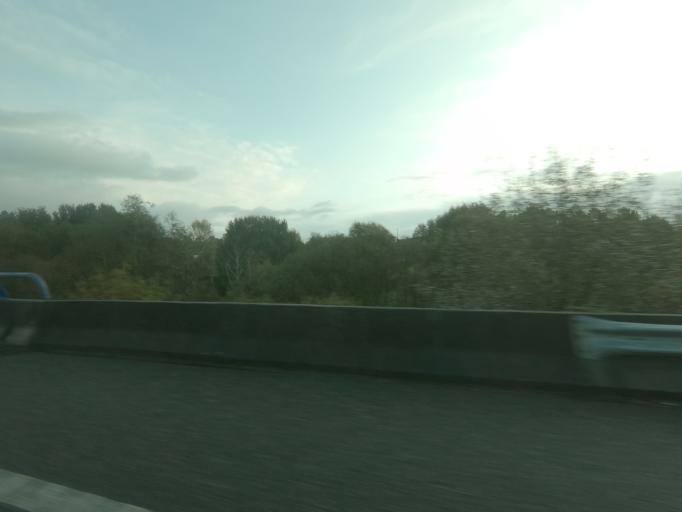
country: ES
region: Galicia
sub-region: Provincia de Pontevedra
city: Tui
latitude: 42.0957
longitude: -8.6437
